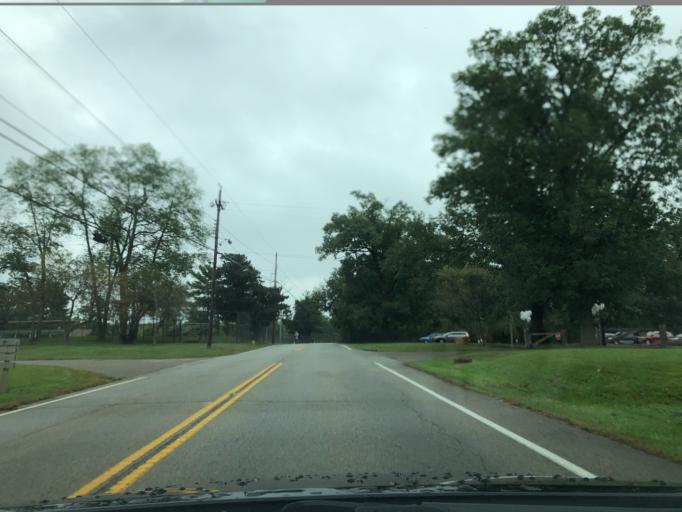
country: US
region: Ohio
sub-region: Hamilton County
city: Sharonville
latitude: 39.2856
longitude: -84.3872
